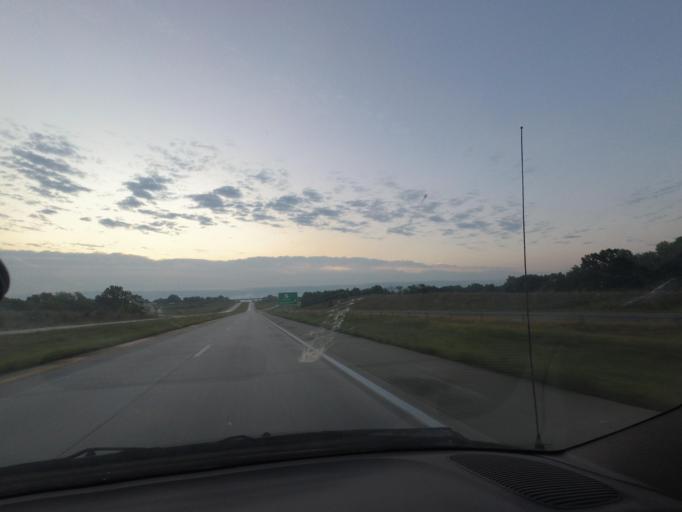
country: US
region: Missouri
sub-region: Macon County
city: Macon
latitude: 39.7568
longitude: -92.6344
